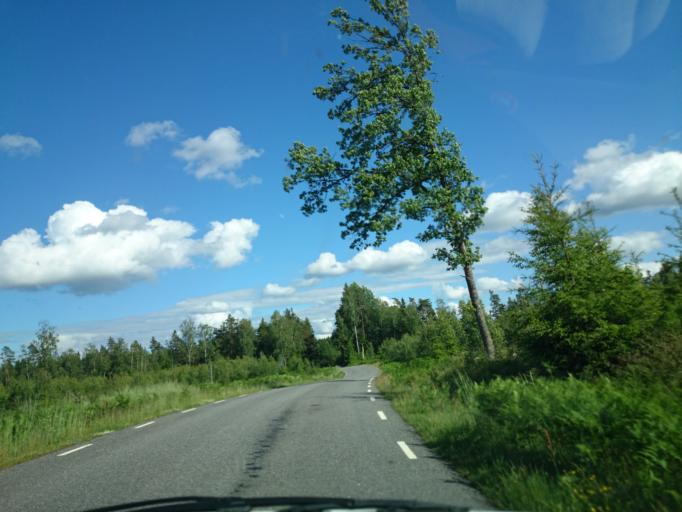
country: SE
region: Kronoberg
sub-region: Ljungby Kommun
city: Lagan
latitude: 57.0158
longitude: 13.9124
